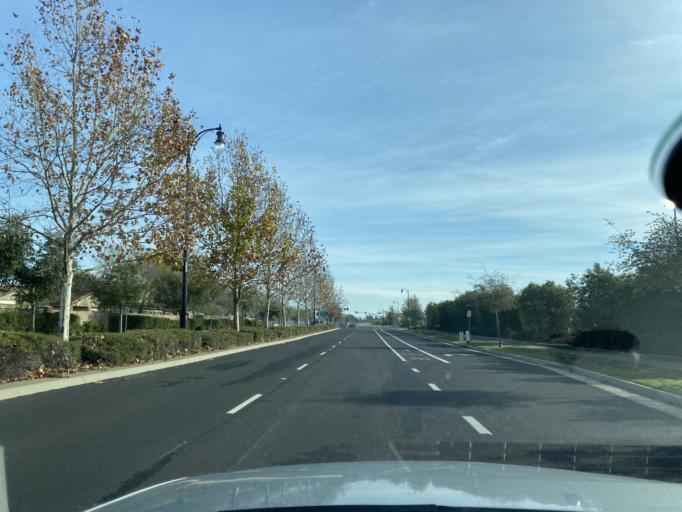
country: US
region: California
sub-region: Sacramento County
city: Elk Grove
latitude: 38.4014
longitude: -121.3978
